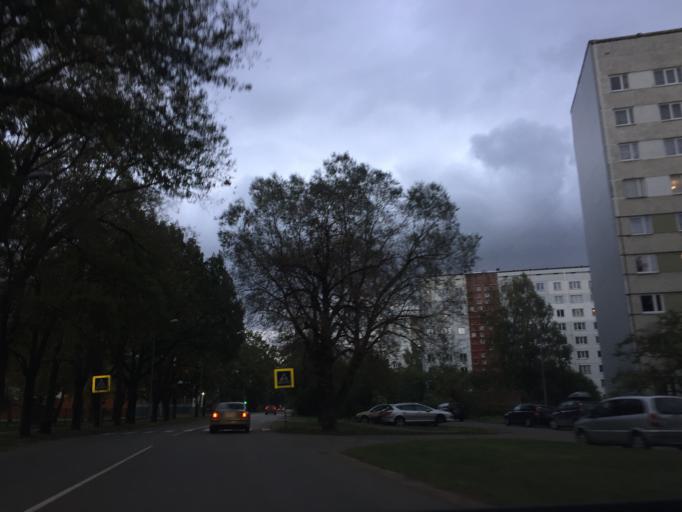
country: LV
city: Tireli
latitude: 56.9540
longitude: 23.6076
